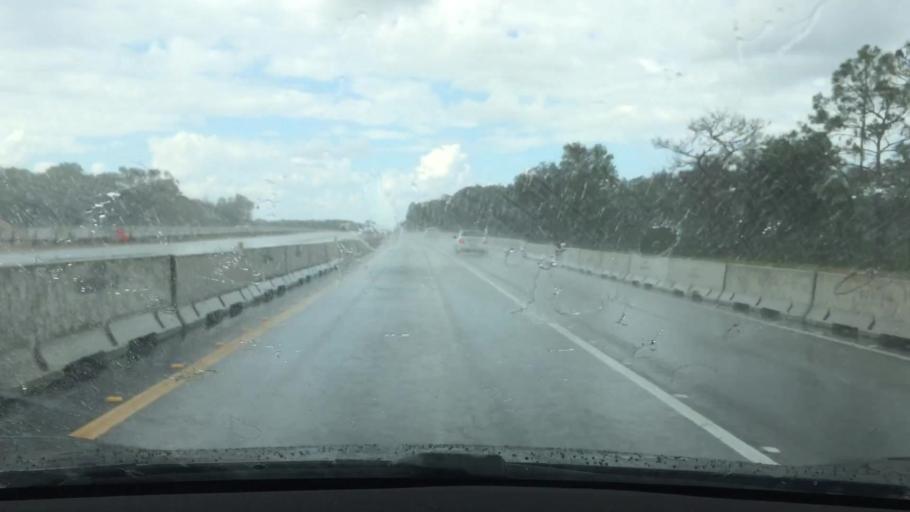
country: US
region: Florida
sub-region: Orange County
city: Wedgefield
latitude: 28.4517
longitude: -81.1036
